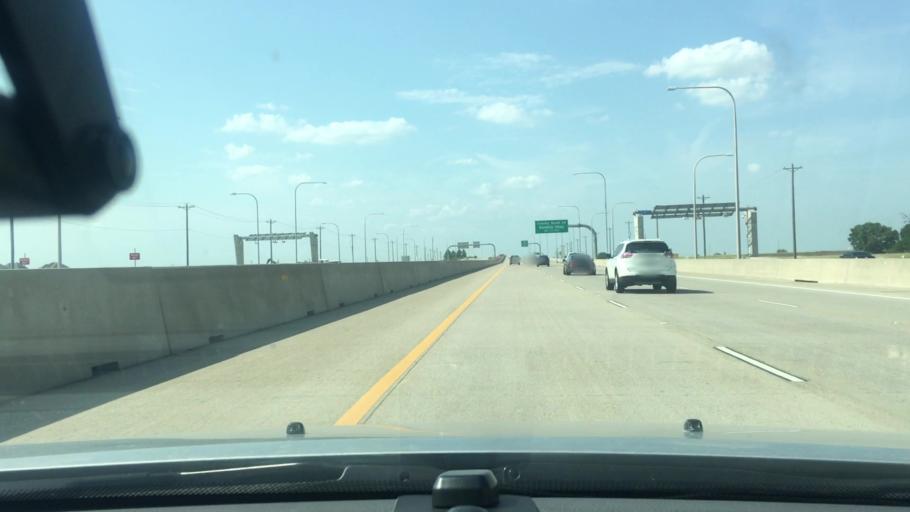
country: US
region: Texas
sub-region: Collin County
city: Frisco
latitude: 33.1835
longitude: -96.8392
